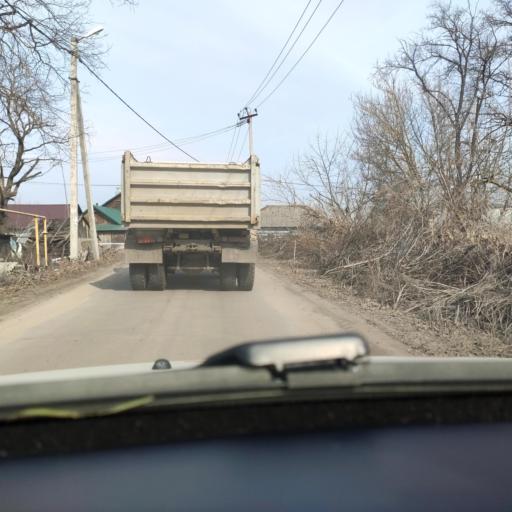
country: RU
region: Voronezj
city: Ramon'
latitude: 51.9041
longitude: 39.3642
